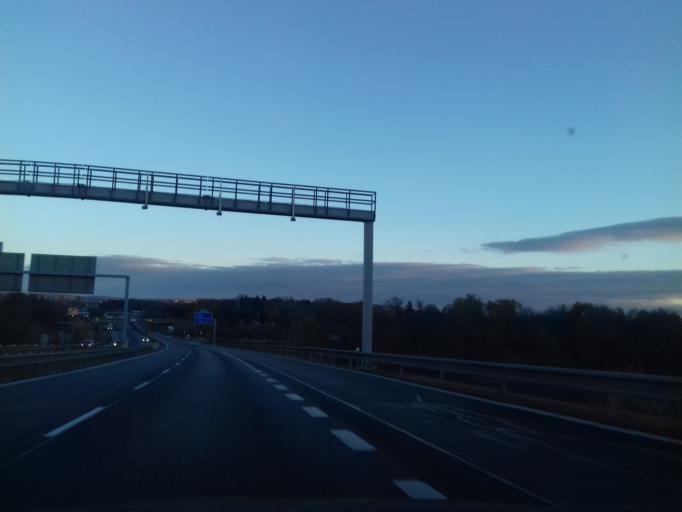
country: CZ
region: South Moravian
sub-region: Okres Vyskov
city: Vyskov
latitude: 49.2776
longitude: 17.0214
